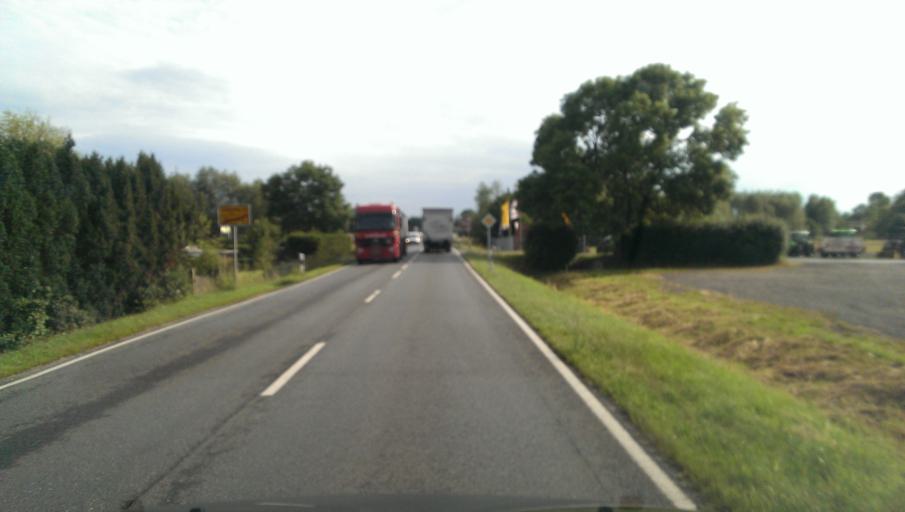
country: DE
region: Saxony-Anhalt
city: Zeitz
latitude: 51.0848
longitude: 12.1657
